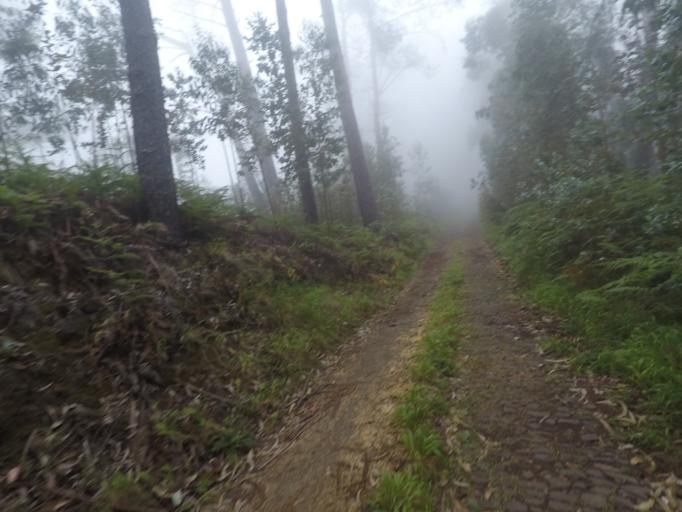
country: PT
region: Madeira
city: Ponta do Sol
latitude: 32.7187
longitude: -17.0929
